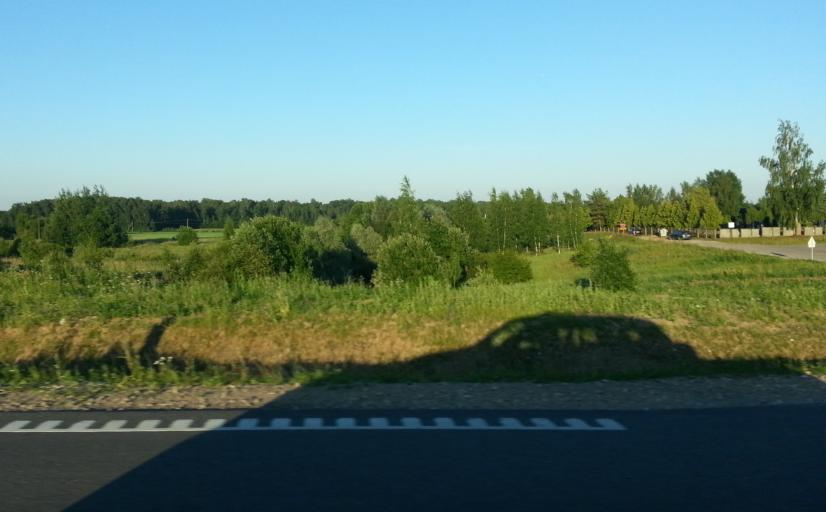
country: LT
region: Panevezys
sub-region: Panevezys City
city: Panevezys
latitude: 55.6501
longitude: 24.3552
